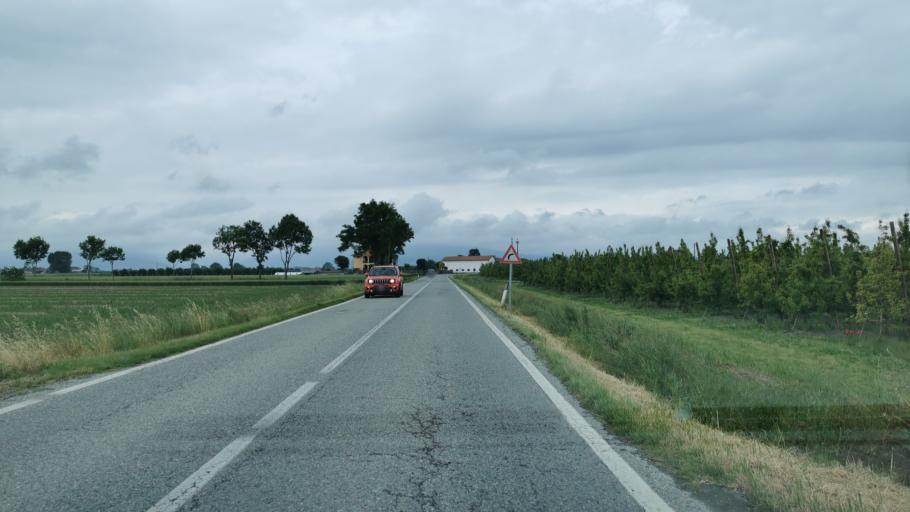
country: IT
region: Piedmont
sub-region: Provincia di Cuneo
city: Vottignasco
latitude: 44.6051
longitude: 7.5964
